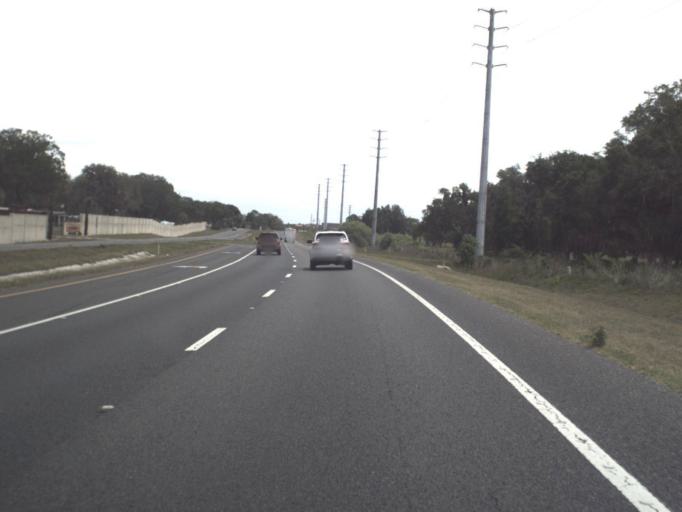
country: US
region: Florida
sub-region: Sumter County
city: Wildwood
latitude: 28.8234
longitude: -81.9844
